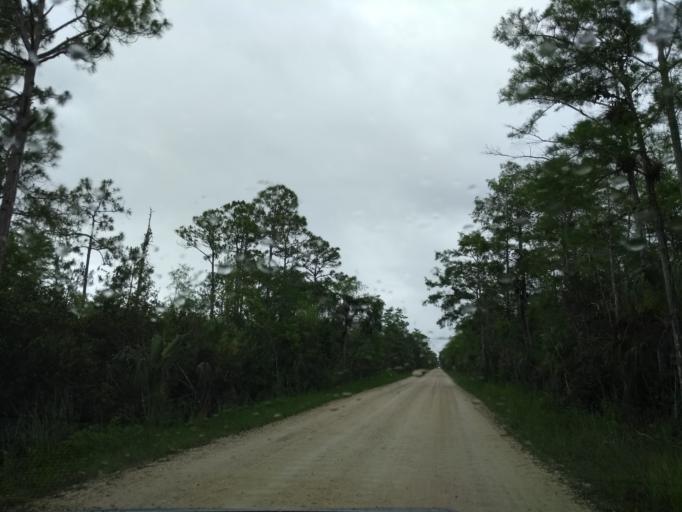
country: US
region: Florida
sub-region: Miami-Dade County
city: The Hammocks
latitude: 25.7605
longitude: -81.0032
